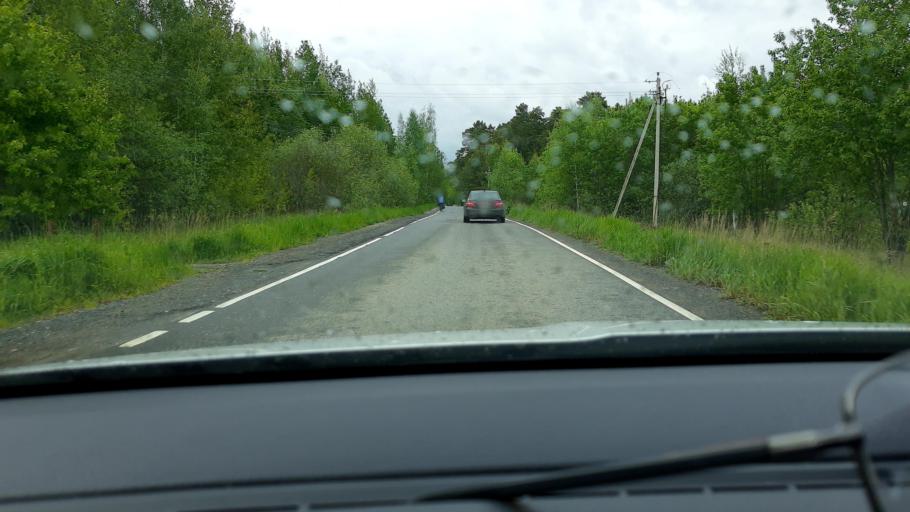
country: RU
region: Moskovskaya
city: Nikolina Gora
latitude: 55.7578
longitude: 36.9813
